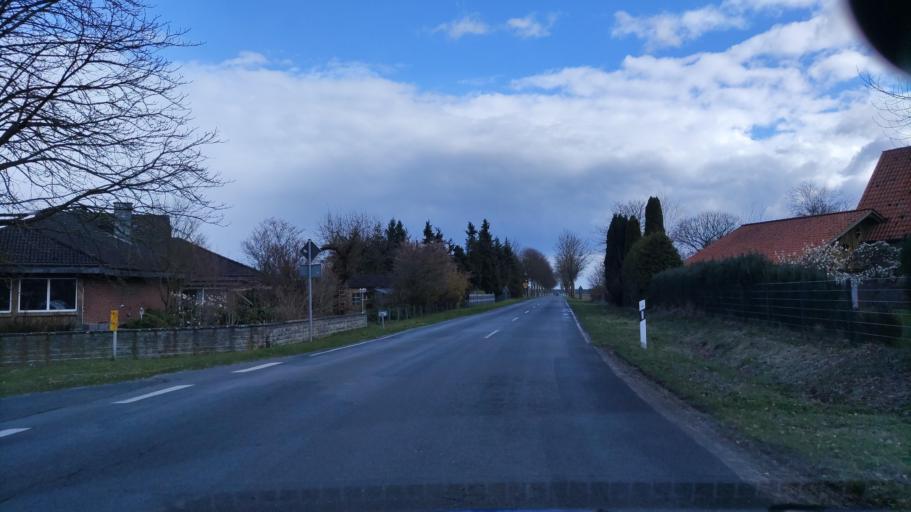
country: DE
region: Lower Saxony
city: Hermannsburg
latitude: 52.8118
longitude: 10.0637
